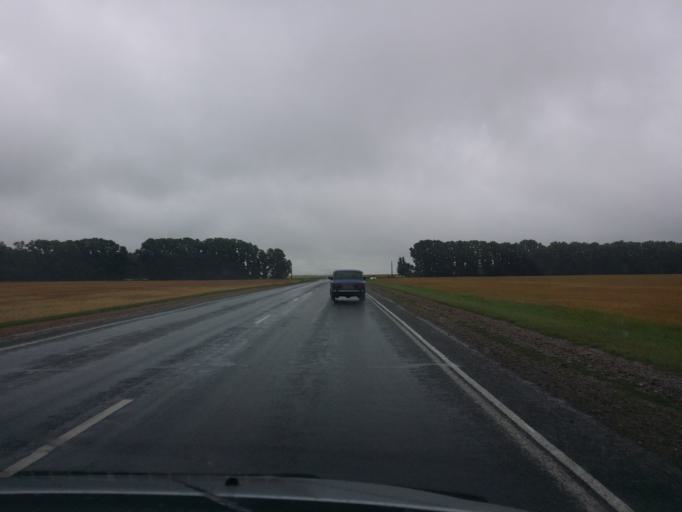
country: RU
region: Altai Krai
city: Bayunovskiye Klyuchi
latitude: 53.2713
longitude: 84.3795
